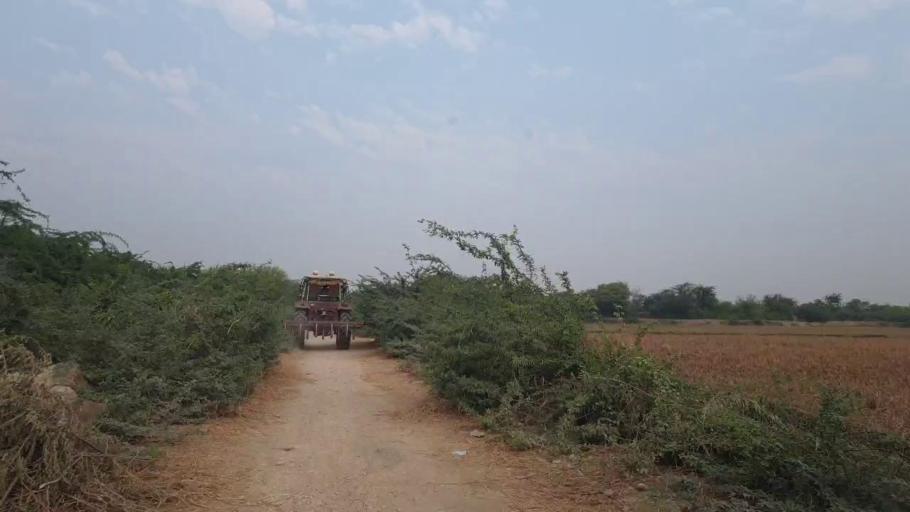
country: PK
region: Sindh
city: Tando Bago
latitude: 24.7936
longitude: 68.8772
